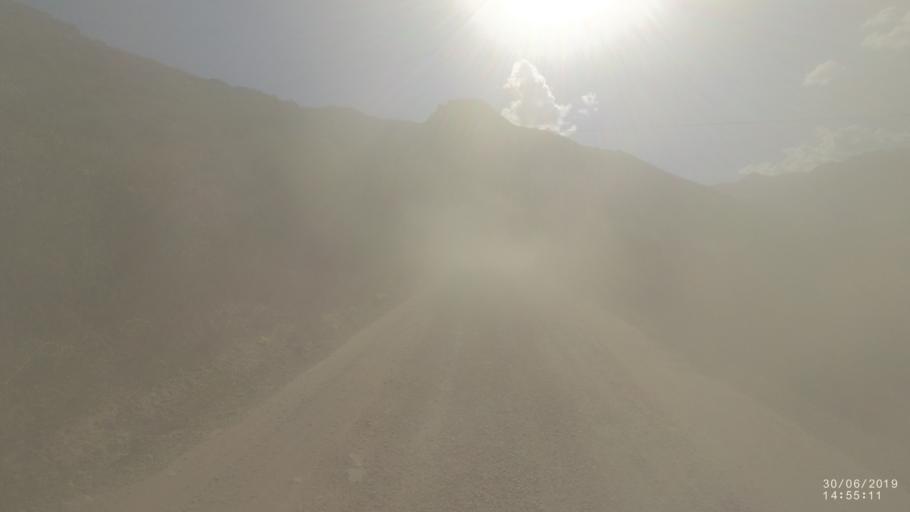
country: BO
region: Cochabamba
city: Irpa Irpa
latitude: -17.7553
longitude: -66.3518
